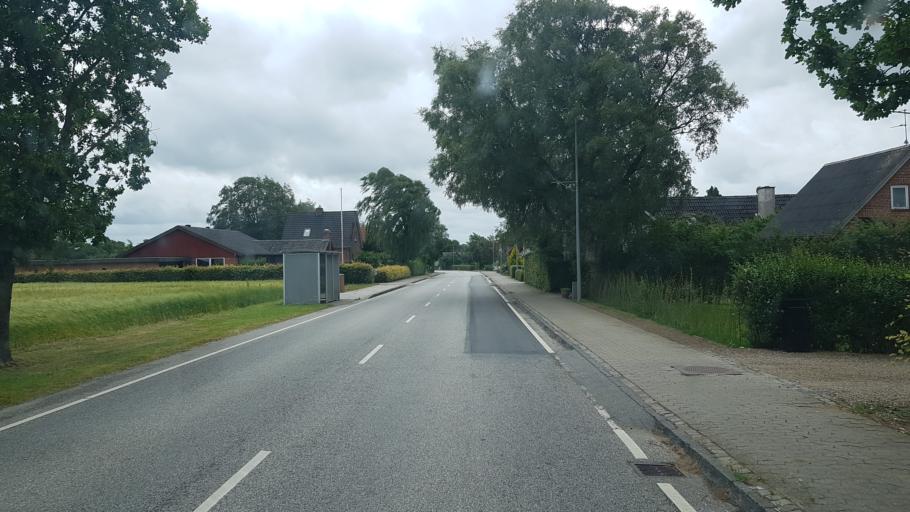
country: DK
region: South Denmark
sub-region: Vejen Kommune
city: Rodding
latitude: 55.3329
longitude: 9.0568
